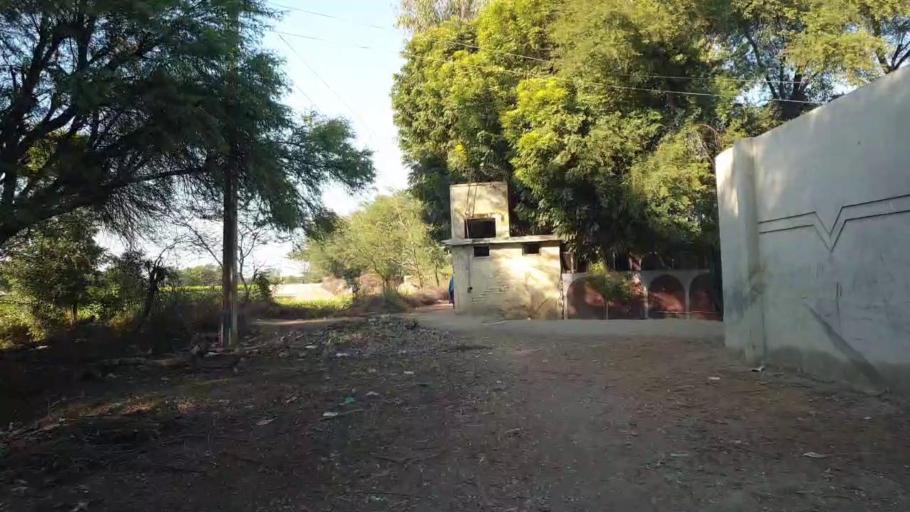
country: PK
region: Sindh
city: Shahpur Chakar
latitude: 26.1223
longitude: 68.5635
